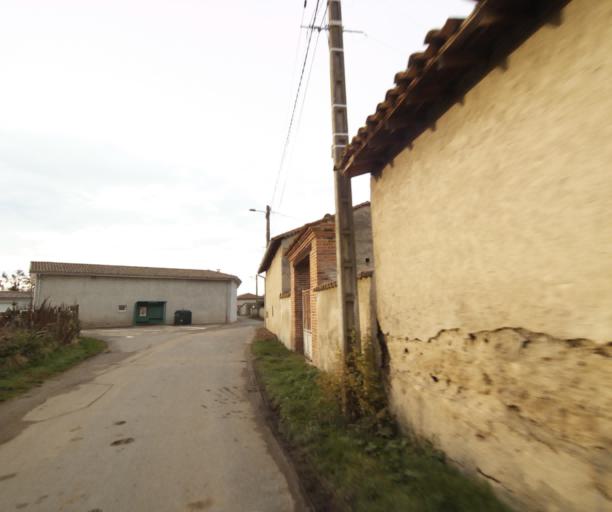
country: FR
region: Rhone-Alpes
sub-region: Departement de la Loire
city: Sury-le-Comtal
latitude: 45.5291
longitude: 4.1659
